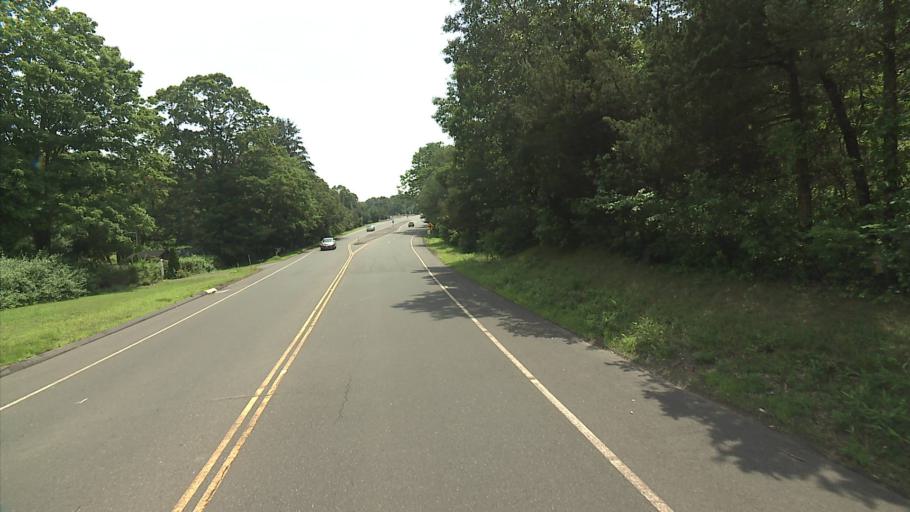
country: US
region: Connecticut
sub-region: New Haven County
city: Madison
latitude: 41.2934
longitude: -72.5737
